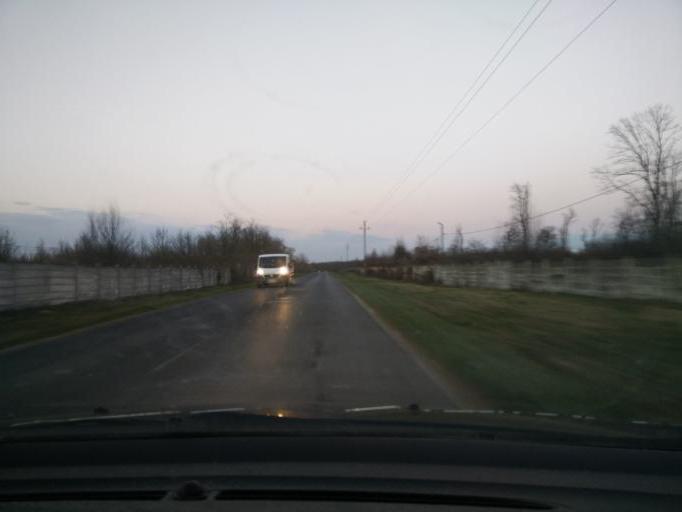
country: HU
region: Veszprem
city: Devecser
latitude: 47.0834
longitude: 17.4043
